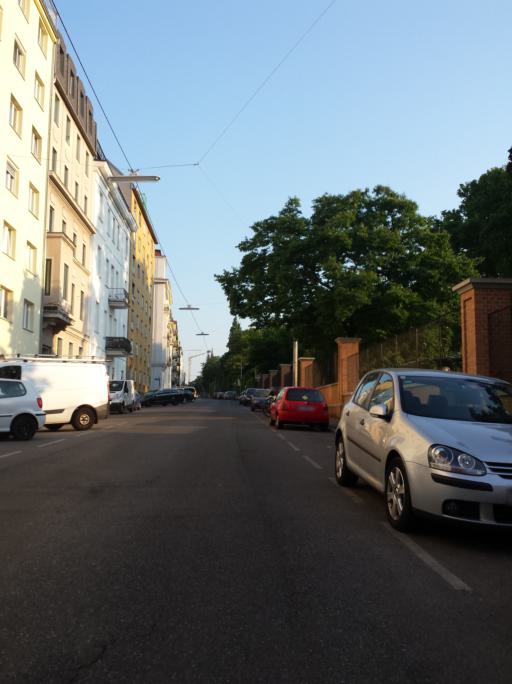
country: AT
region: Vienna
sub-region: Wien Stadt
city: Vienna
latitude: 48.1939
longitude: 16.3852
